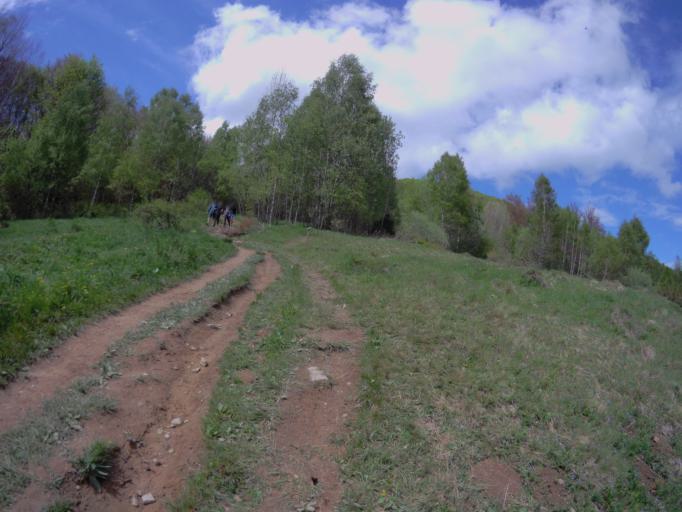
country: PL
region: Subcarpathian Voivodeship
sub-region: Powiat bieszczadzki
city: Lutowiska
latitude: 49.1428
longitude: 22.5666
